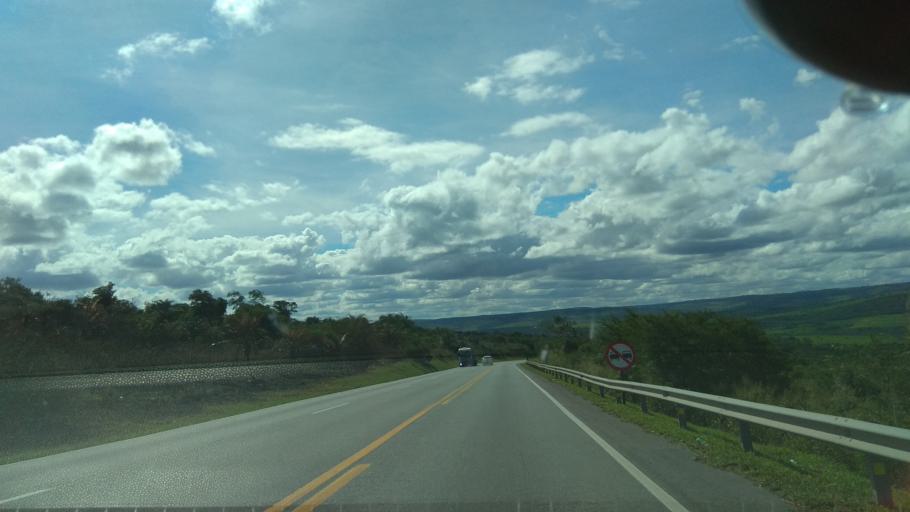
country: BR
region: Bahia
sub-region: Santa Ines
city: Santa Ines
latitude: -13.1861
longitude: -40.0061
